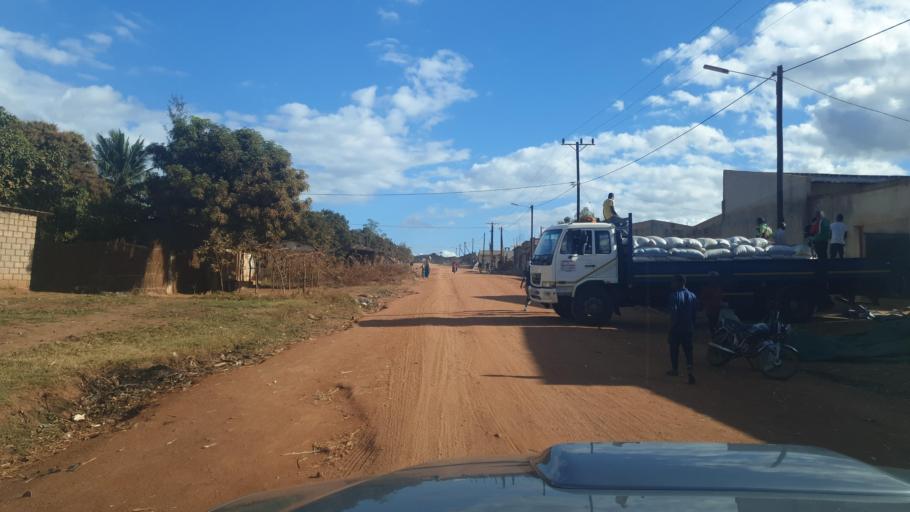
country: MZ
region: Nampula
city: Nampula
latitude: -15.0999
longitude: 39.2228
